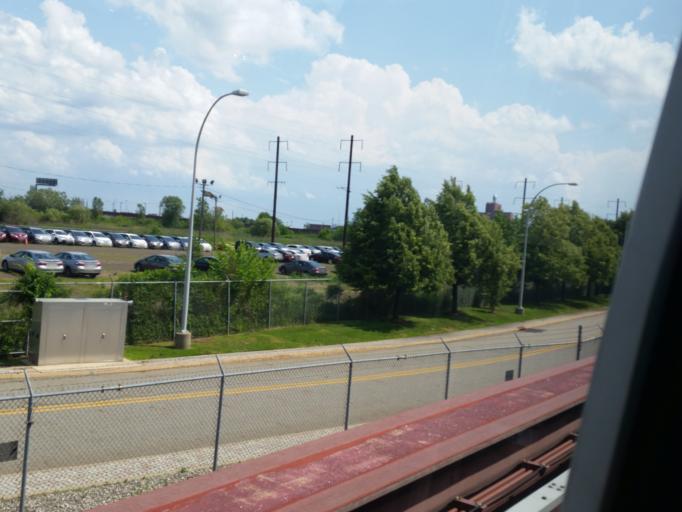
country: US
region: New Jersey
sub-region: Union County
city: Hillside
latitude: 40.7017
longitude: -74.1917
